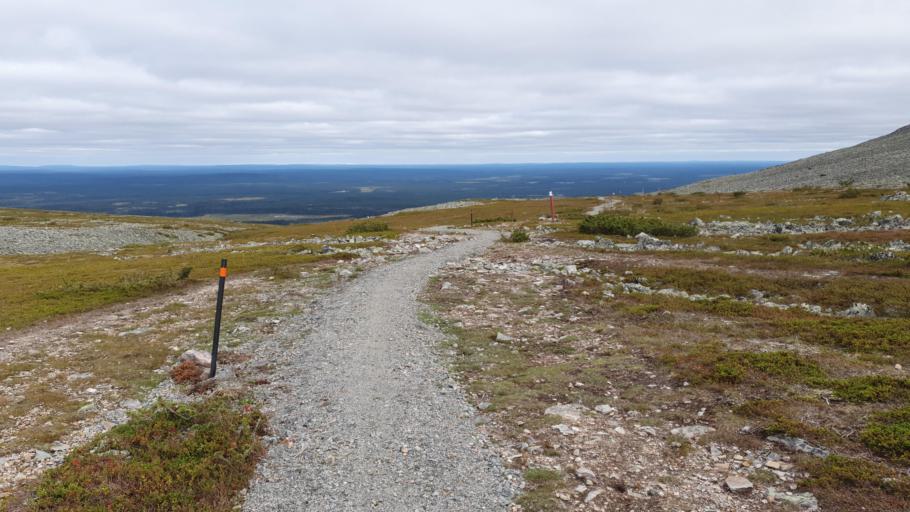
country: FI
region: Lapland
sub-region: Tunturi-Lappi
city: Kolari
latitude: 67.5699
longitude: 24.2317
